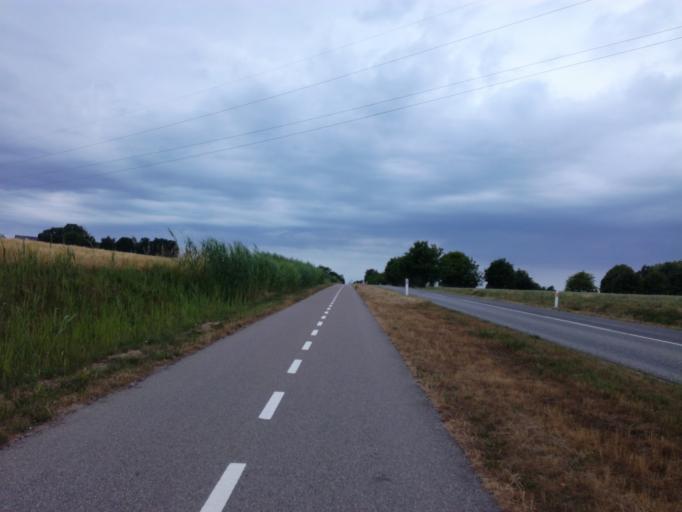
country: DK
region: South Denmark
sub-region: Vejle Kommune
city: Borkop
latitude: 55.6596
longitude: 9.6320
